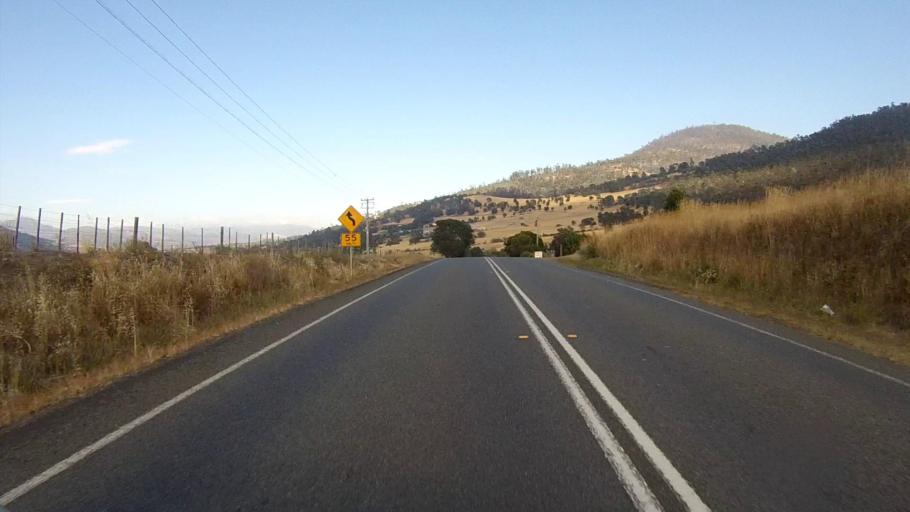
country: AU
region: Tasmania
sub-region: Glenorchy
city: Granton
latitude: -42.7484
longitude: 147.1564
